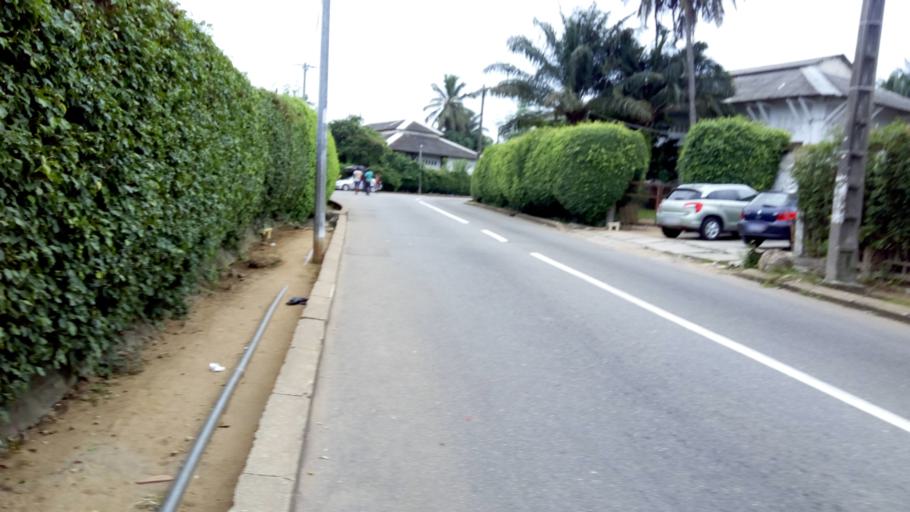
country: CI
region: Lagunes
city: Abidjan
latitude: 5.3225
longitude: -4.0238
